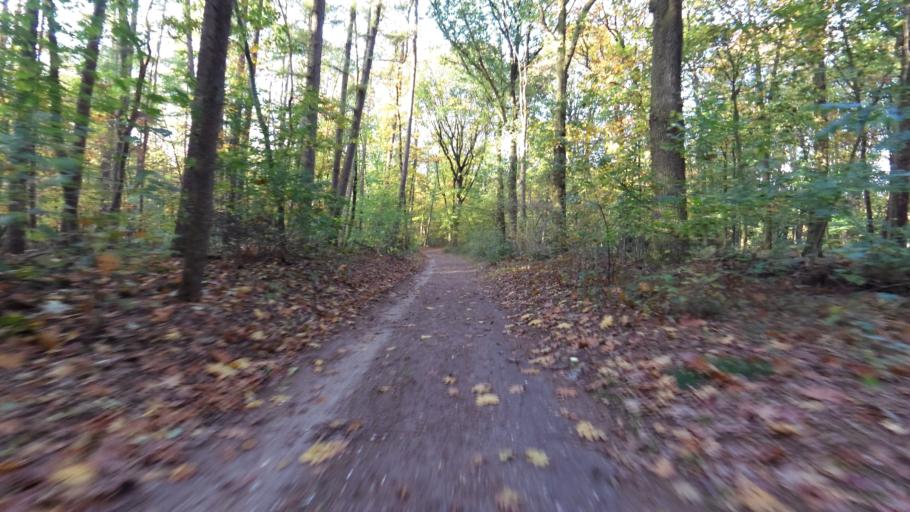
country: NL
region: Gelderland
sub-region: Gemeente Ede
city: Lunteren
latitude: 52.0881
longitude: 5.6429
